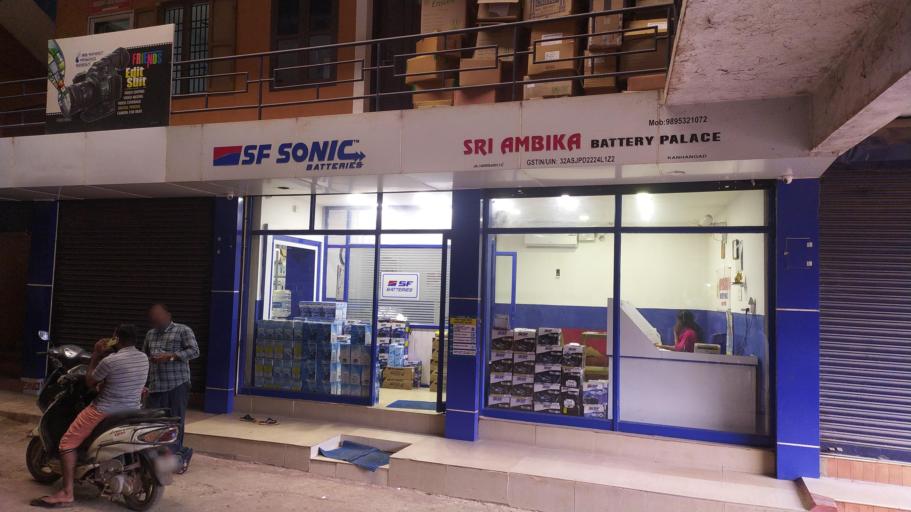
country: IN
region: Kerala
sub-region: Kasaragod District
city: Kannangad
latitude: 12.3228
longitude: 75.0890
